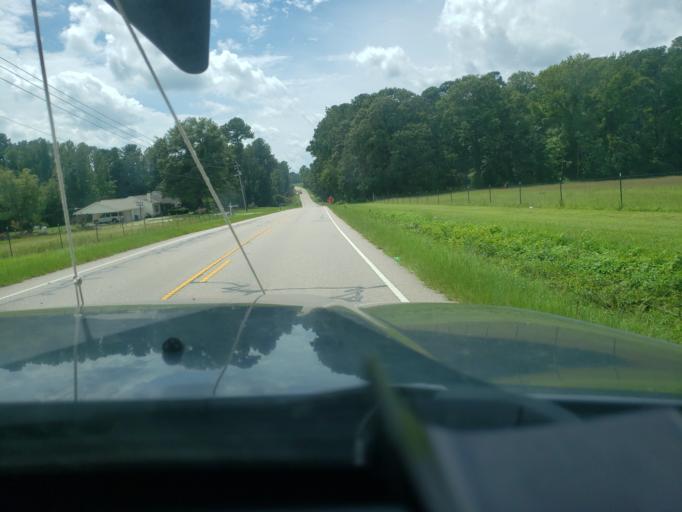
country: US
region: North Carolina
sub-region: Wake County
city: Rolesville
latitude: 35.8892
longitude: -78.4341
